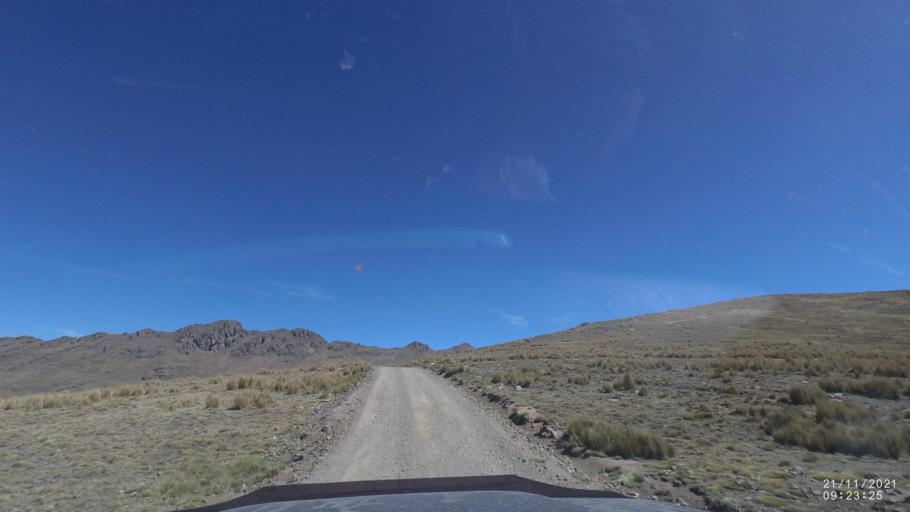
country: BO
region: Cochabamba
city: Cochabamba
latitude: -17.0976
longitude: -66.2529
